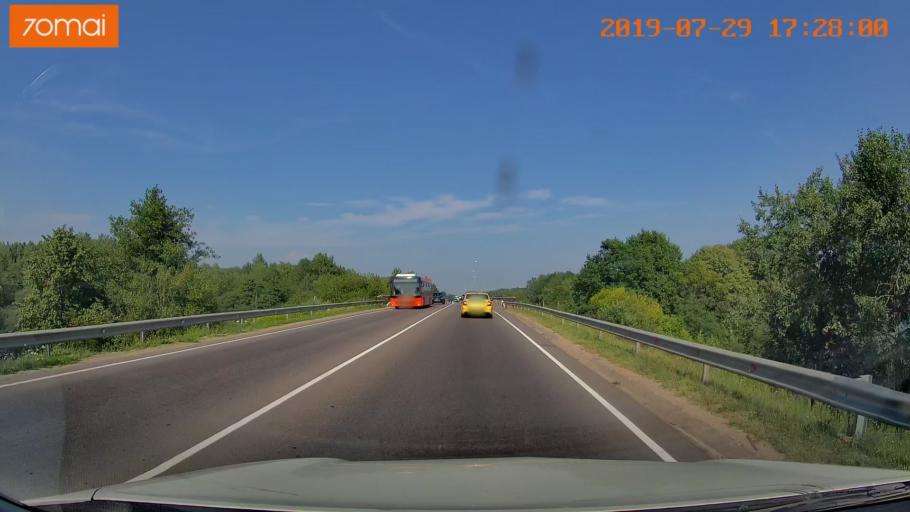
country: RU
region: Kaliningrad
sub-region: Gorod Kaliningrad
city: Kaliningrad
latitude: 54.7615
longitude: 20.4624
